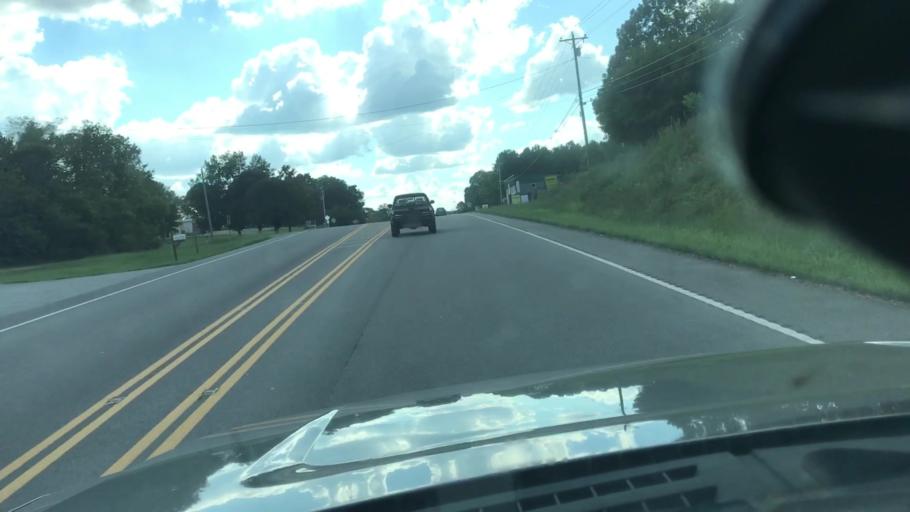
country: US
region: Tennessee
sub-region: Williamson County
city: Fairview
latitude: 35.9865
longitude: -87.1073
